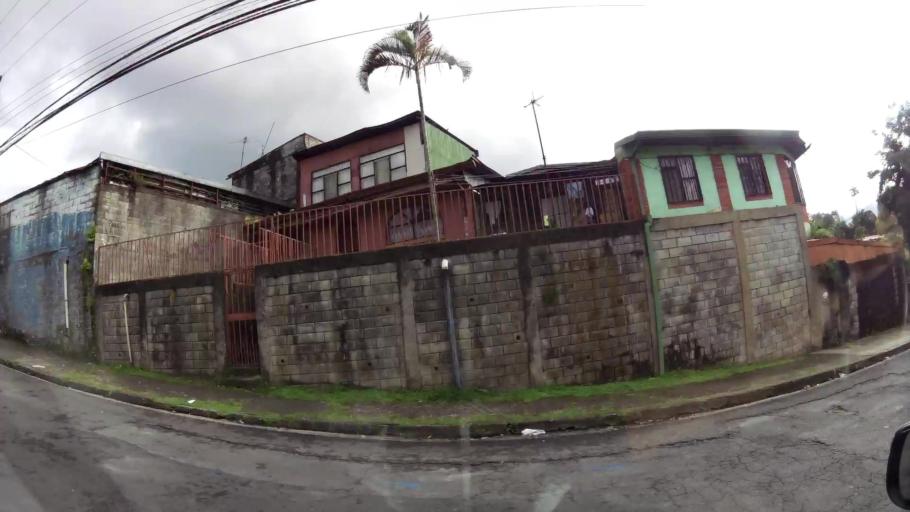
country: CR
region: San Jose
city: Curridabat
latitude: 9.9094
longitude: -84.0420
